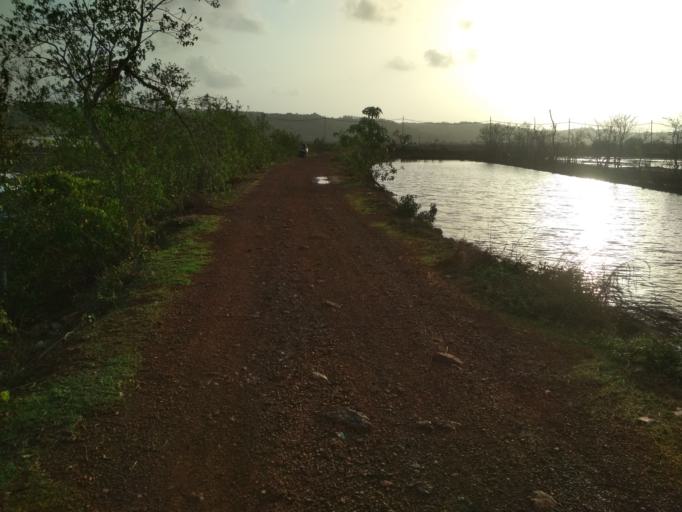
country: IN
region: Goa
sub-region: North Goa
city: Serula
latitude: 15.5289
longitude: 73.8590
